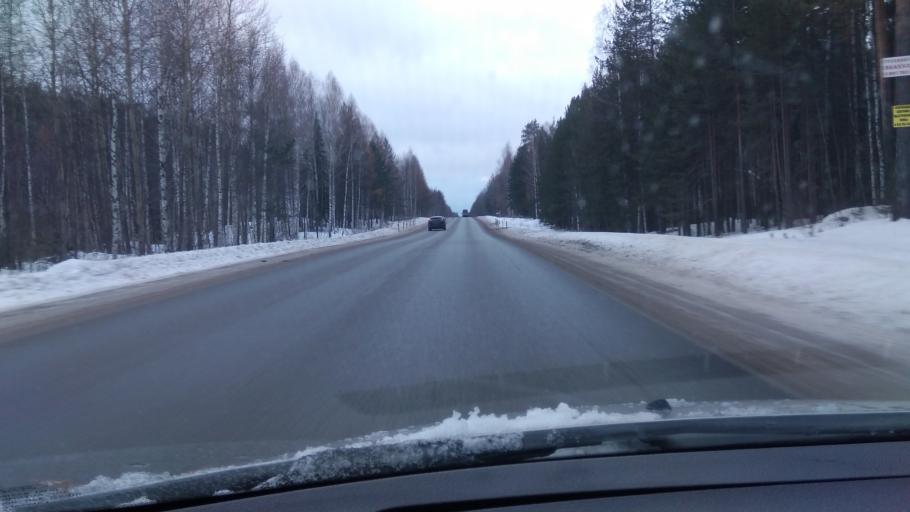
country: RU
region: Sverdlovsk
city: Iset'
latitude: 57.1094
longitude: 60.3432
